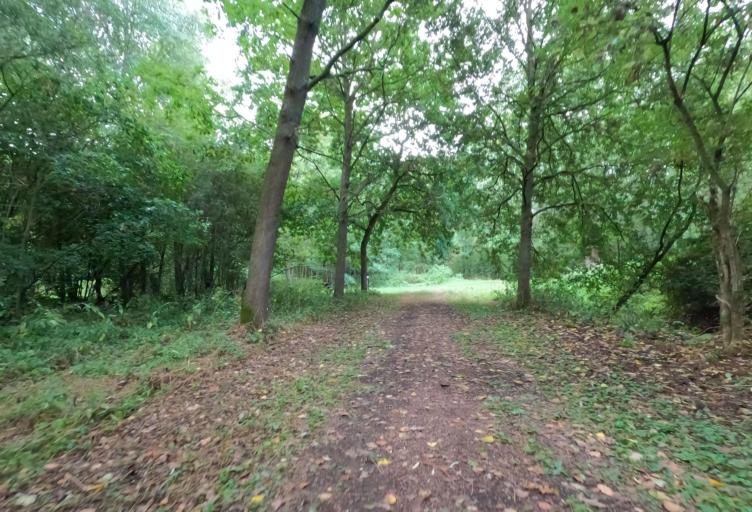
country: BE
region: Flanders
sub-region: Provincie Antwerpen
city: Puurs
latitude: 51.0696
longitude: 4.2655
